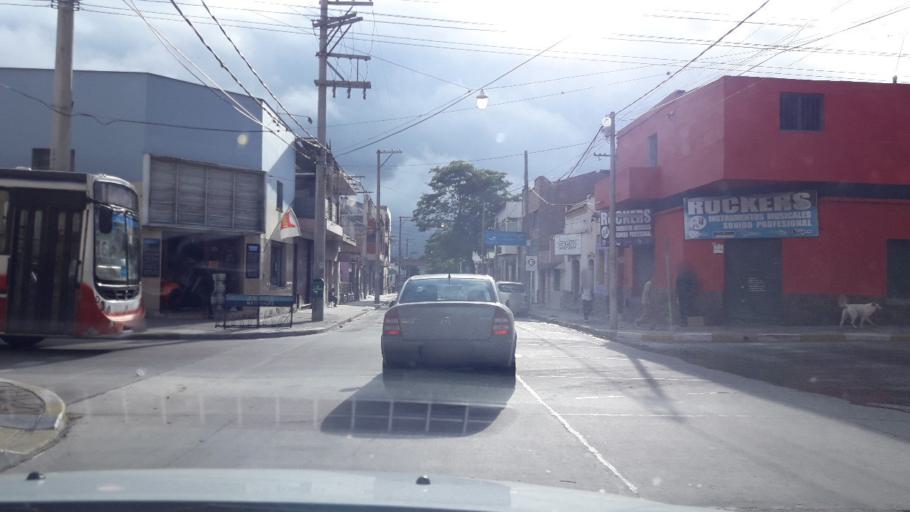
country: AR
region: Jujuy
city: San Salvador de Jujuy
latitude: -24.1908
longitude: -65.3050
